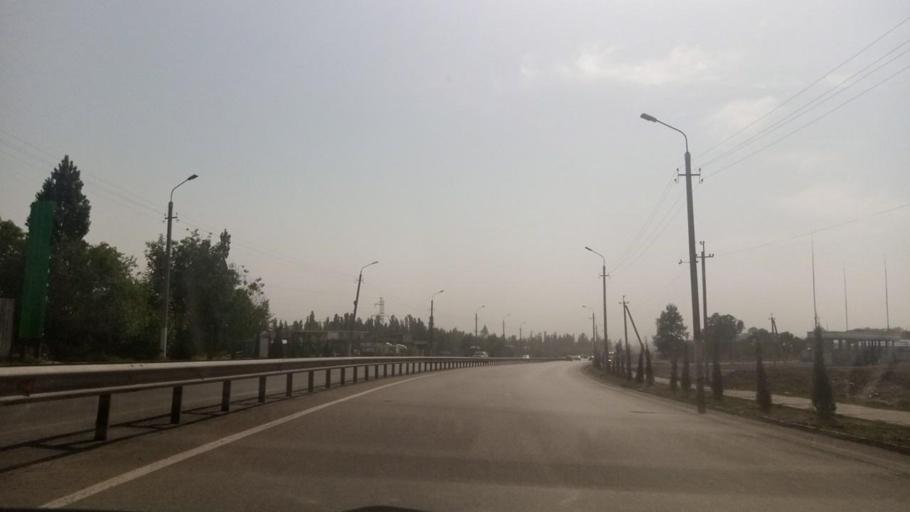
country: UZ
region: Toshkent
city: Angren
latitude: 41.0262
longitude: 70.1354
